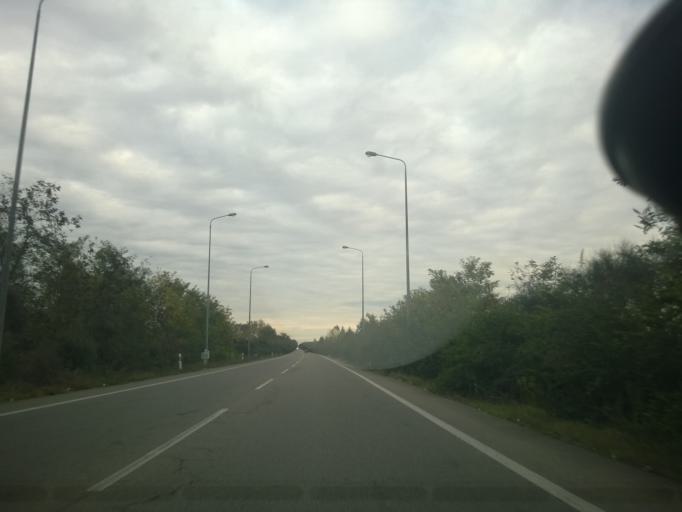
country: GR
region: Central Macedonia
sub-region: Nomos Pellis
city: Karyotissa
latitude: 40.7780
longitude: 22.3230
